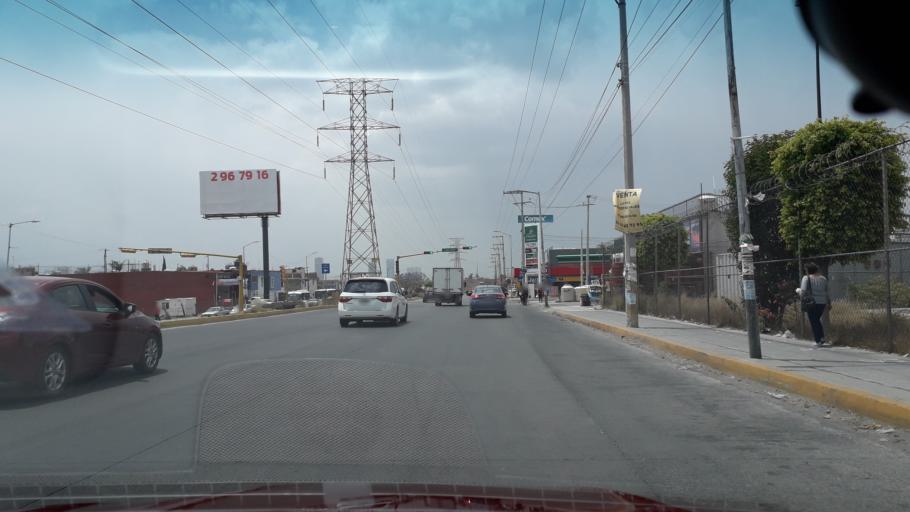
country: MX
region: Puebla
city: Tlazcalancingo
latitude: 19.0054
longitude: -98.2398
